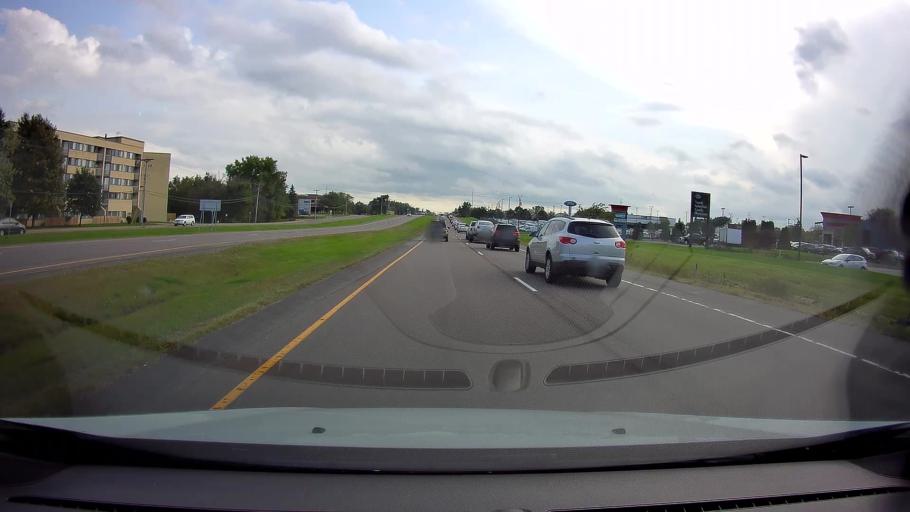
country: US
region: Minnesota
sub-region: Ramsey County
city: Roseville
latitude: 45.0268
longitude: -93.1672
